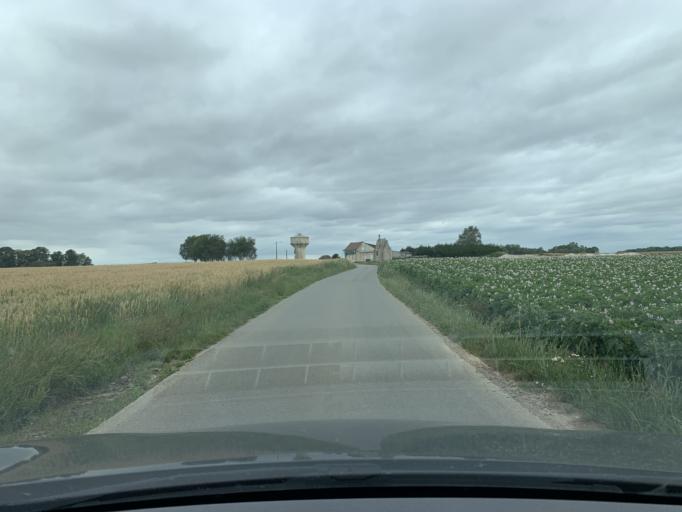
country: FR
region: Nord-Pas-de-Calais
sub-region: Departement du Pas-de-Calais
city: Oisy-le-Verger
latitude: 50.2201
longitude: 3.1177
